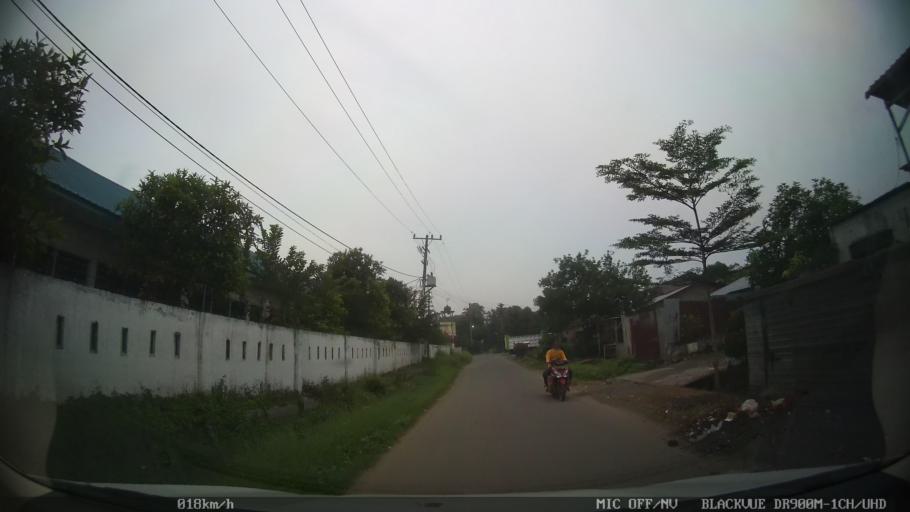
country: ID
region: North Sumatra
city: Deli Tua
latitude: 3.5431
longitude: 98.7292
